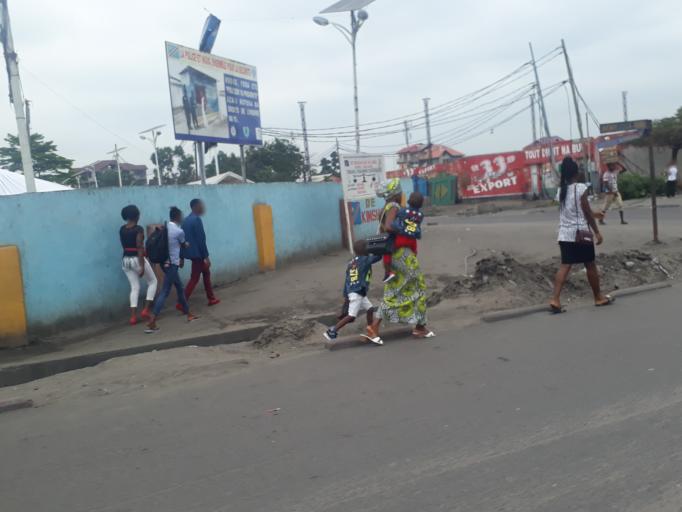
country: CD
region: Kinshasa
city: Kinshasa
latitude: -4.3219
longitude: 15.3119
